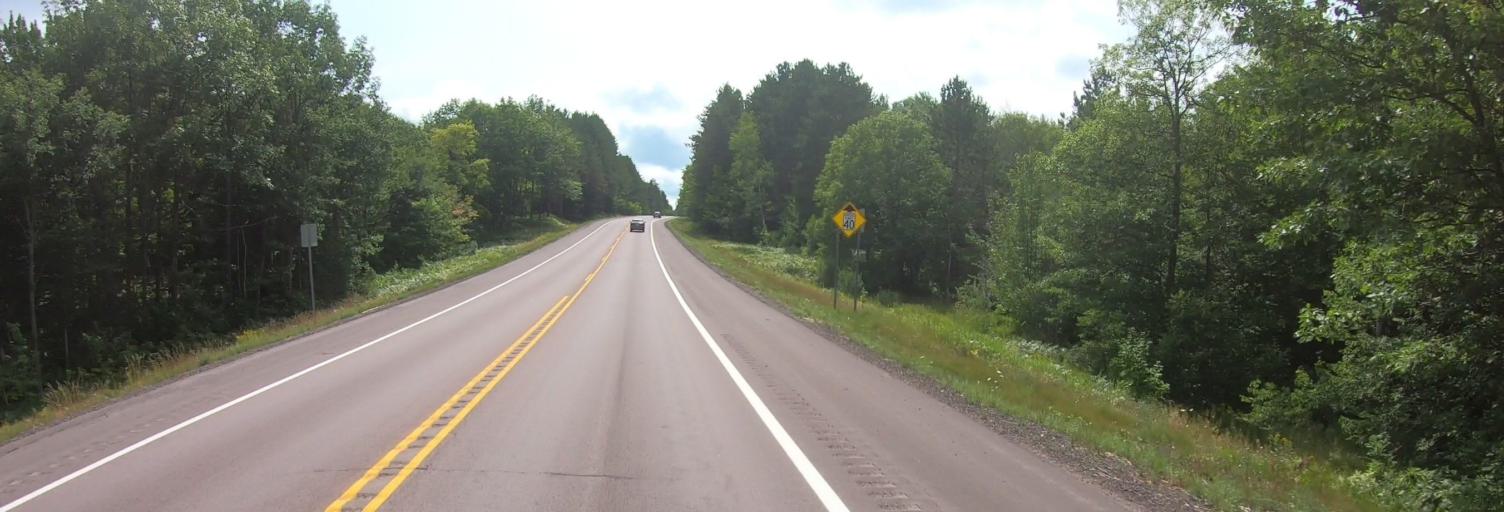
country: US
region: Michigan
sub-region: Houghton County
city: Hancock
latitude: 47.0508
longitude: -88.6684
